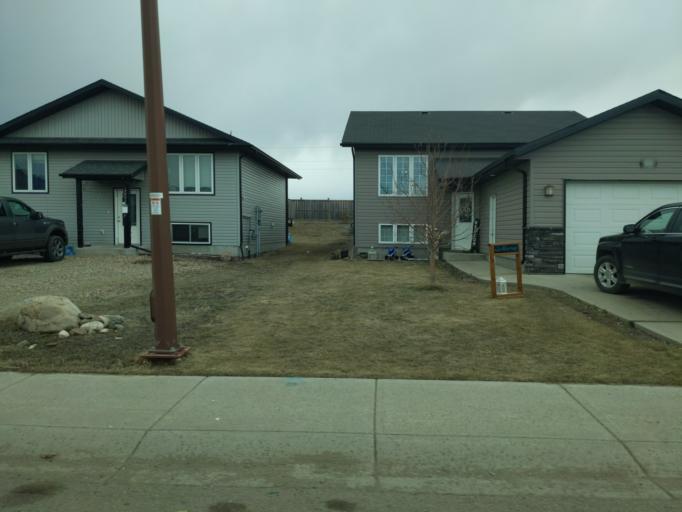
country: CA
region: Saskatchewan
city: Lloydminster
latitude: 53.2720
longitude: -110.0530
